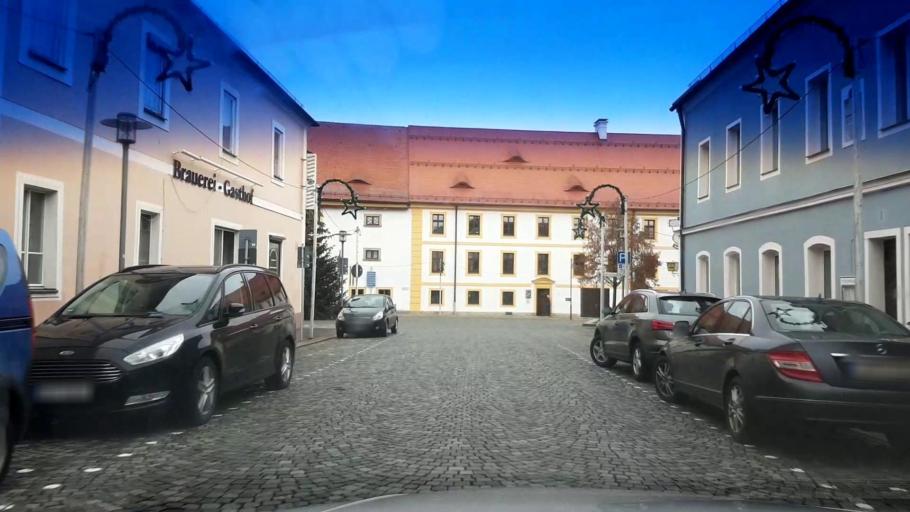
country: DE
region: Bavaria
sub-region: Upper Palatinate
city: Waldsassen
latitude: 50.0041
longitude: 12.3070
